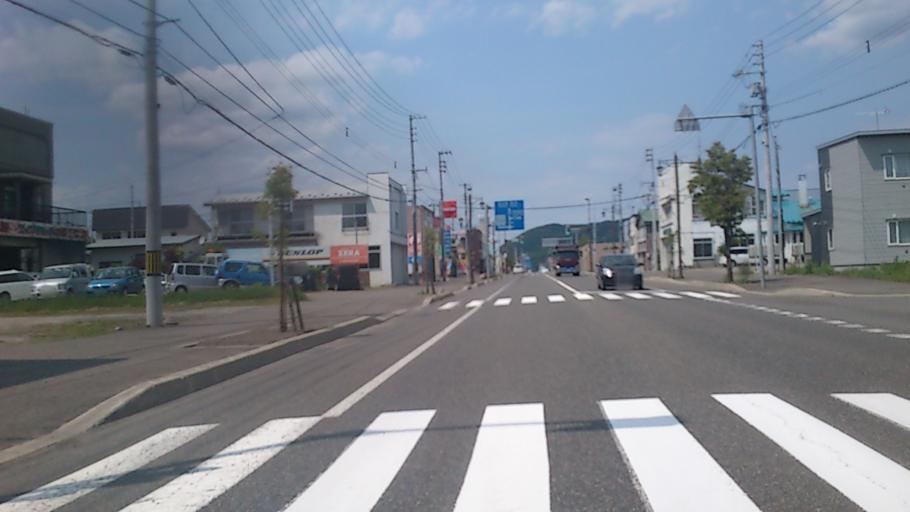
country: JP
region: Hokkaido
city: Otofuke
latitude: 43.2392
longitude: 143.5466
